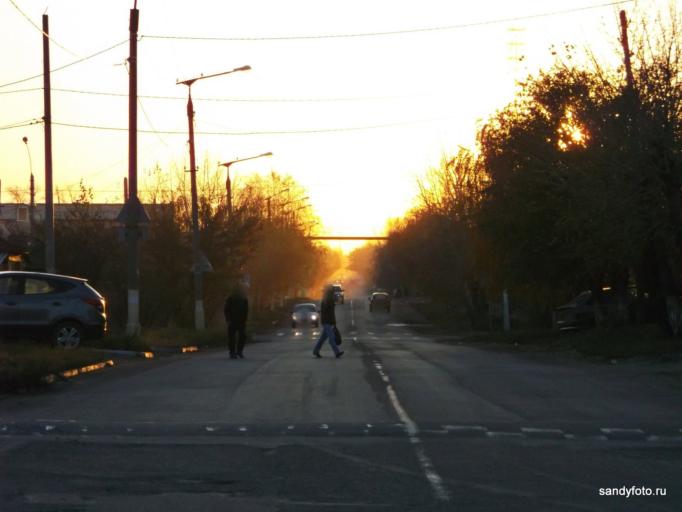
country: RU
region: Chelyabinsk
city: Troitsk
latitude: 54.0880
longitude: 61.5753
